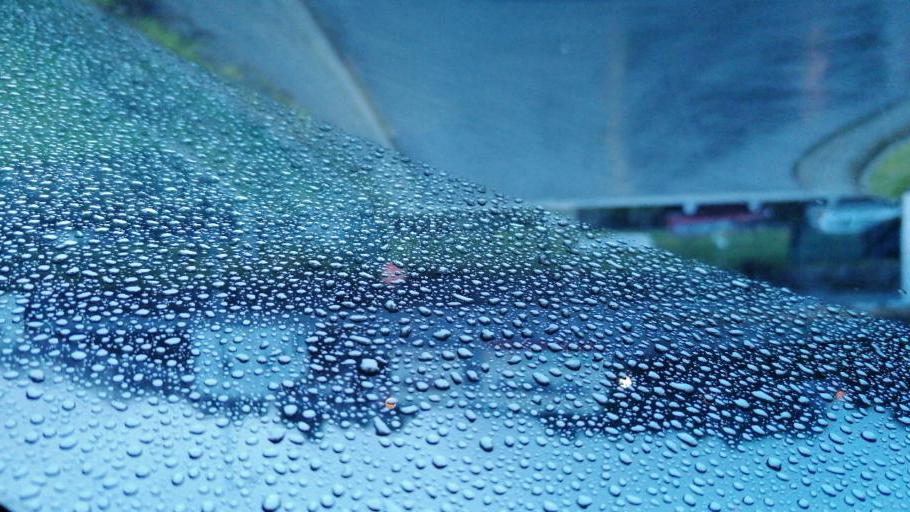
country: PT
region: Vila Real
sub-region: Vila Pouca de Aguiar
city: Vila Pouca de Aguiar
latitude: 41.4927
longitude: -7.6458
